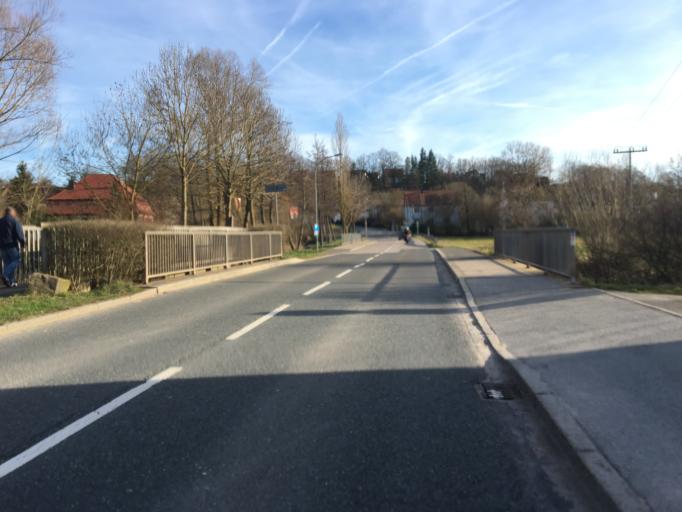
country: DE
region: Bavaria
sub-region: Regierungsbezirk Mittelfranken
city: Wilhermsdorf
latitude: 49.4796
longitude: 10.7179
